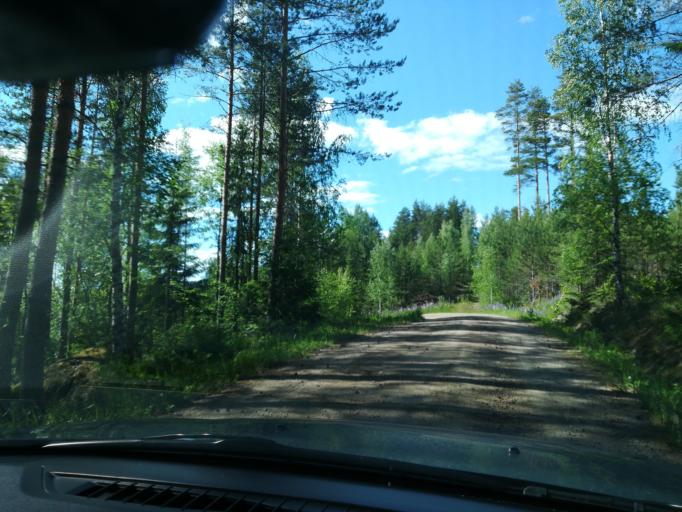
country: FI
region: Southern Savonia
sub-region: Mikkeli
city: Puumala
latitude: 61.6597
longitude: 28.1601
